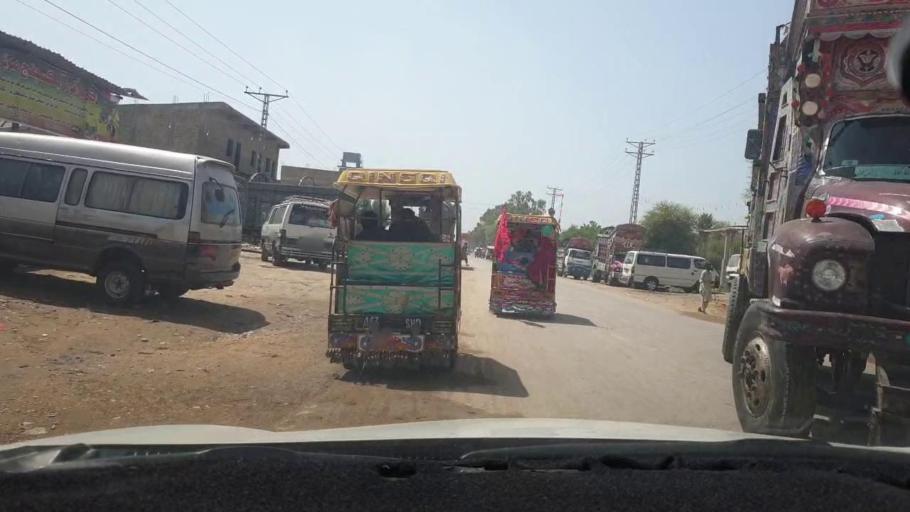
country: PK
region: Sindh
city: Shahdadpur
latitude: 25.9153
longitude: 68.6098
